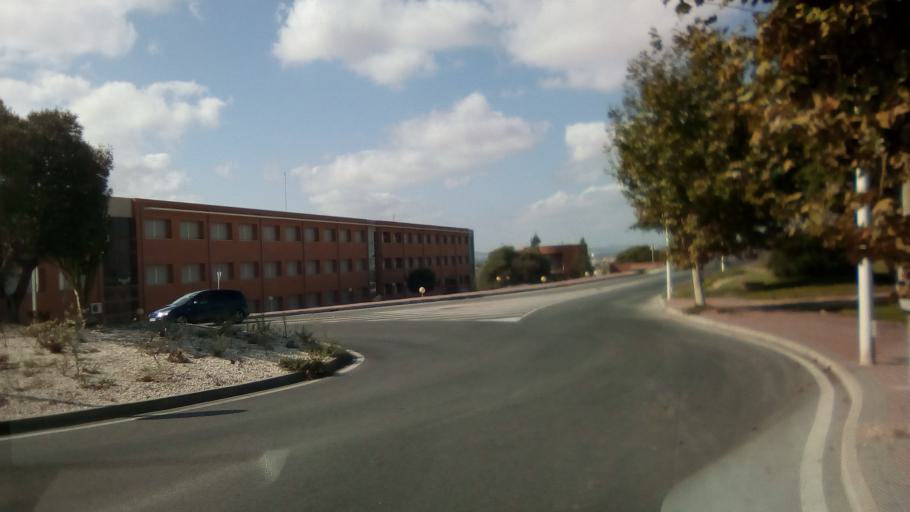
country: ES
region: Valencia
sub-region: Provincia de Alicante
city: Torrevieja
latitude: 37.9994
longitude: -0.6777
